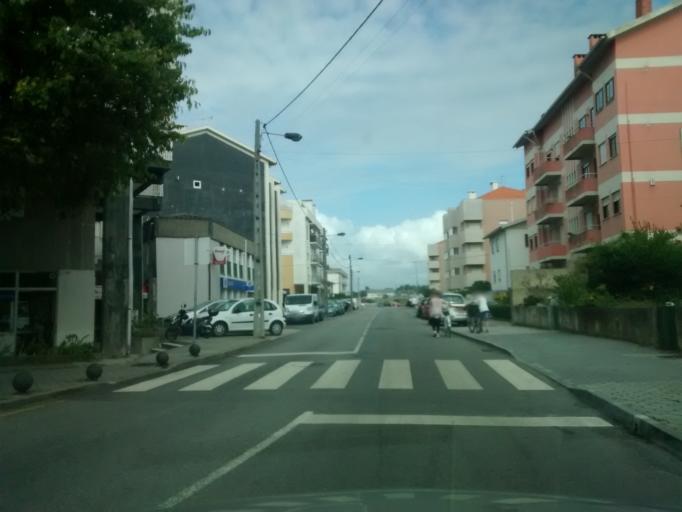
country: PT
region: Aveiro
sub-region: Aveiro
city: Aveiro
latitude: 40.6542
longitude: -8.6232
